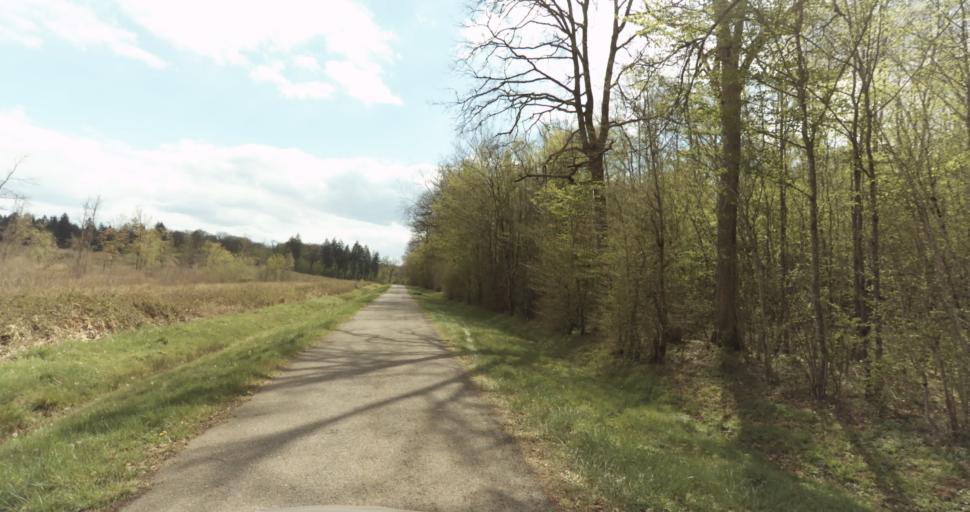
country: FR
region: Bourgogne
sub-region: Departement de la Cote-d'Or
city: Auxonne
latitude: 47.1925
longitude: 5.4521
